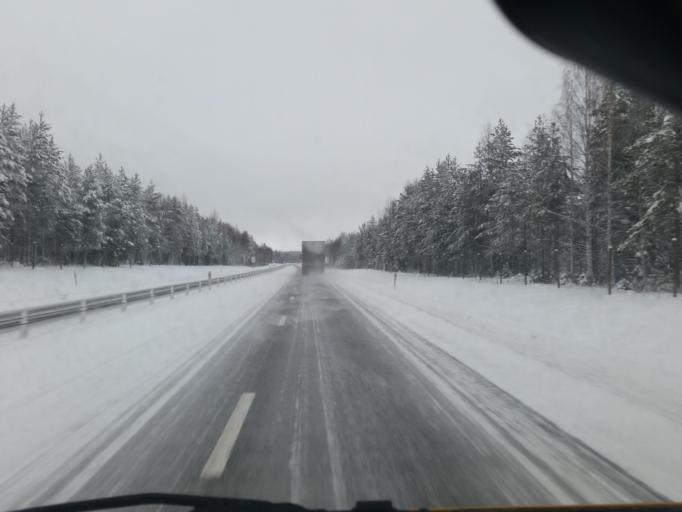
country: SE
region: Norrbotten
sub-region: Pitea Kommun
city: Hortlax
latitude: 65.2898
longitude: 21.4329
